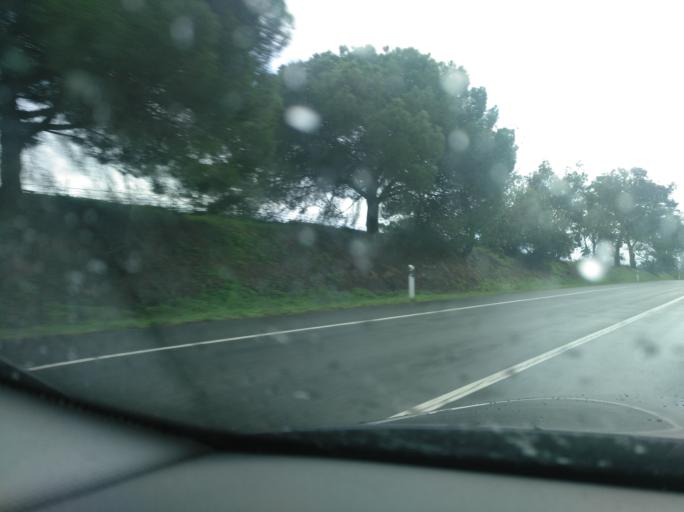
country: PT
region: Setubal
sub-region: Grandola
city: Grandola
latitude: 38.0942
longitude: -8.4184
